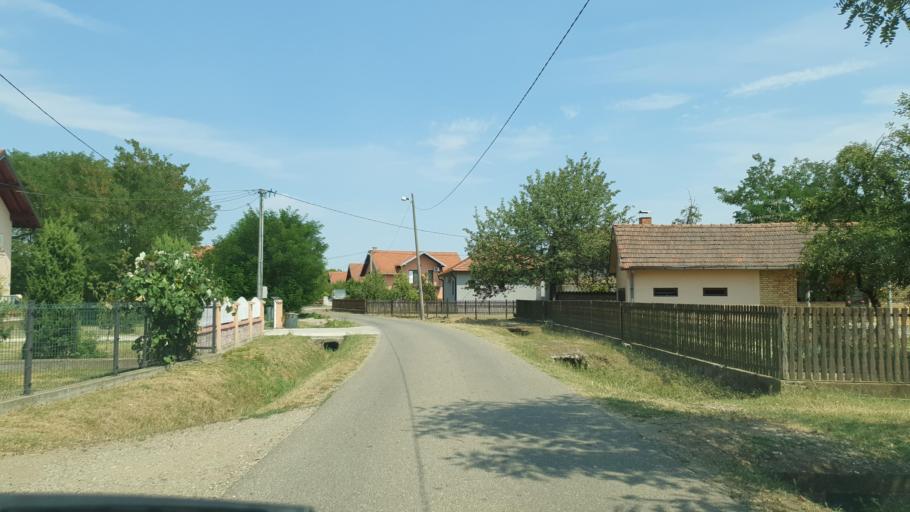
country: BA
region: Republika Srpska
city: Bijeljina
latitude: 44.7255
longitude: 19.2024
